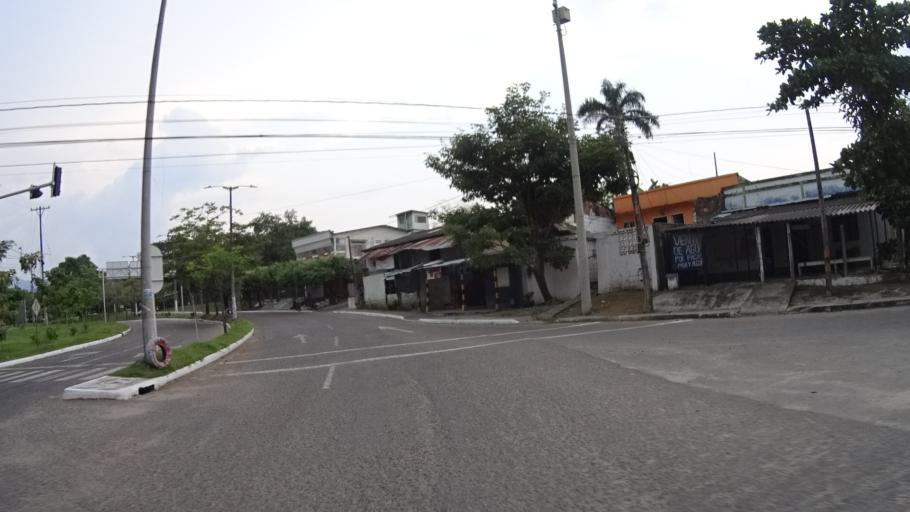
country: CO
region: Cundinamarca
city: Puerto Salgar
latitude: 5.4787
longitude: -74.6717
